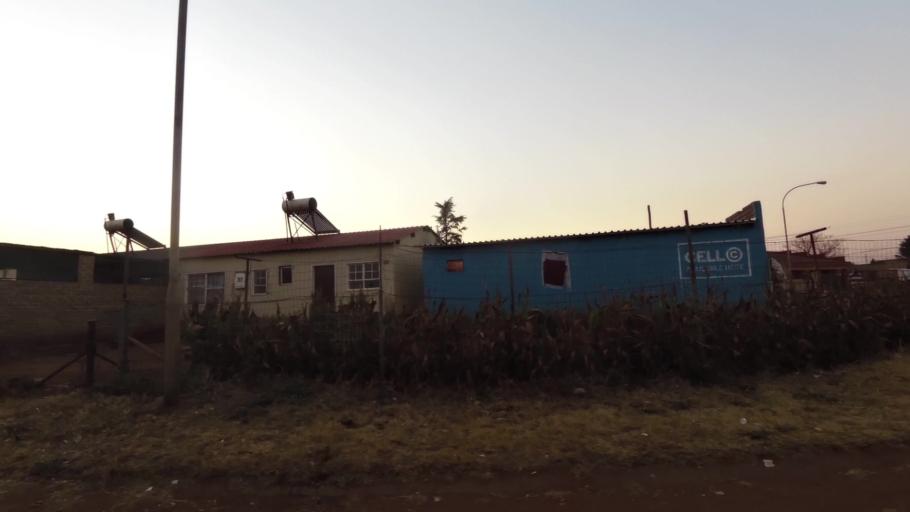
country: ZA
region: Gauteng
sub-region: City of Johannesburg Metropolitan Municipality
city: Soweto
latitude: -26.2940
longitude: 27.8709
